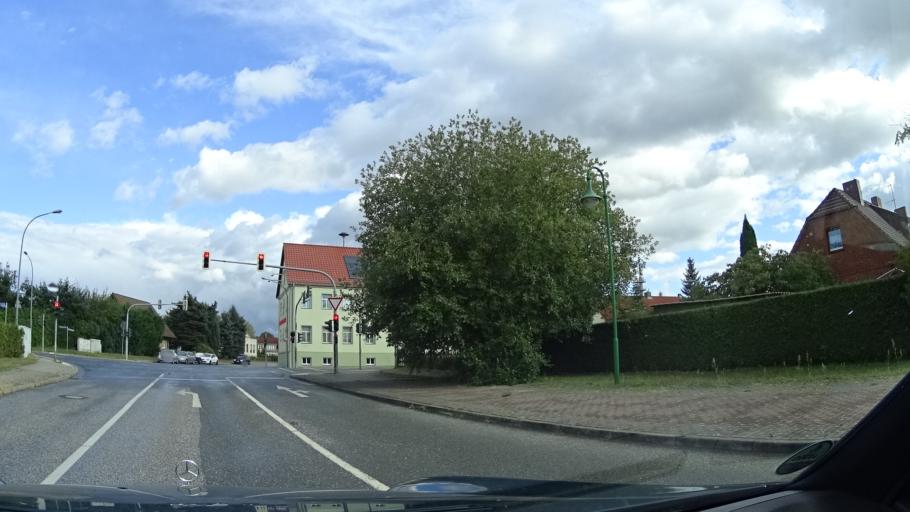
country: DE
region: Brandenburg
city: Neuruppin
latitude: 52.8930
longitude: 12.7974
